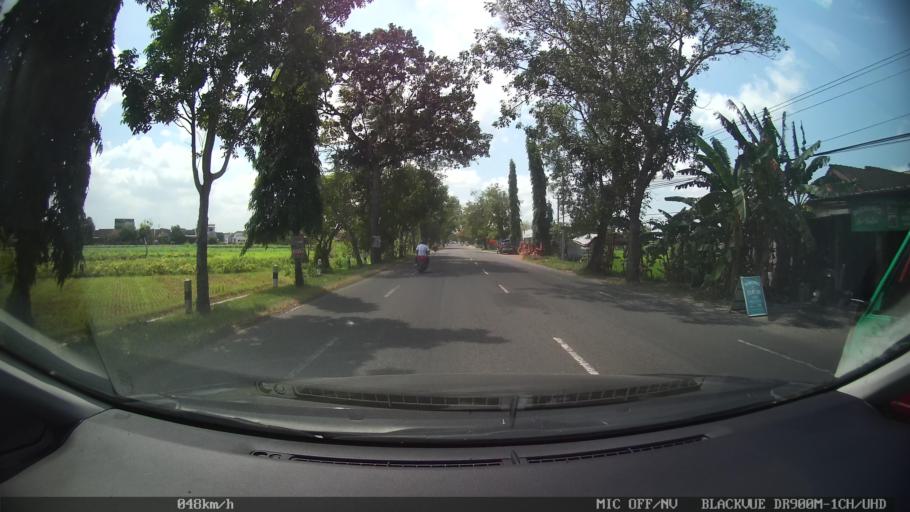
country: ID
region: Daerah Istimewa Yogyakarta
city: Pandak
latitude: -7.9095
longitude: 110.2975
